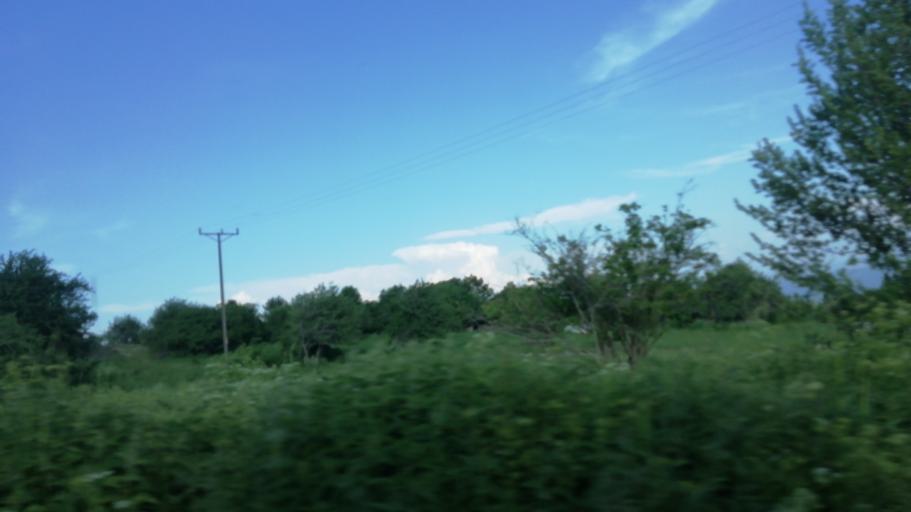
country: TR
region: Karabuk
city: Eskipazar
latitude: 41.0459
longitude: 32.5585
